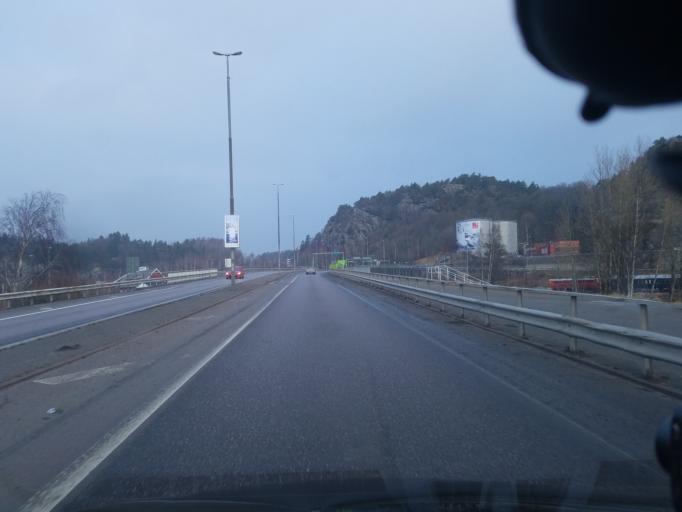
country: SE
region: Vaestra Goetaland
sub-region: Uddevalla Kommun
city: Uddevalla
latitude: 58.3541
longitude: 11.9137
